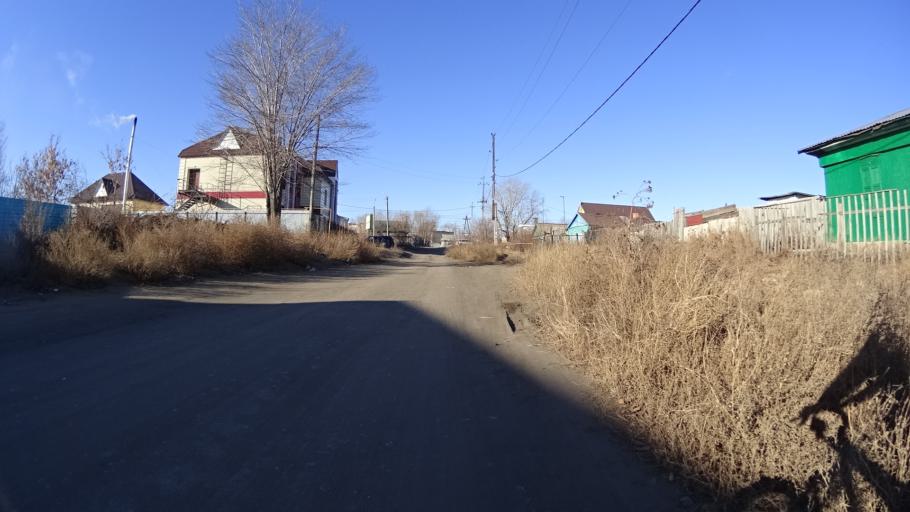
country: RU
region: Chelyabinsk
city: Troitsk
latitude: 54.0938
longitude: 61.5804
